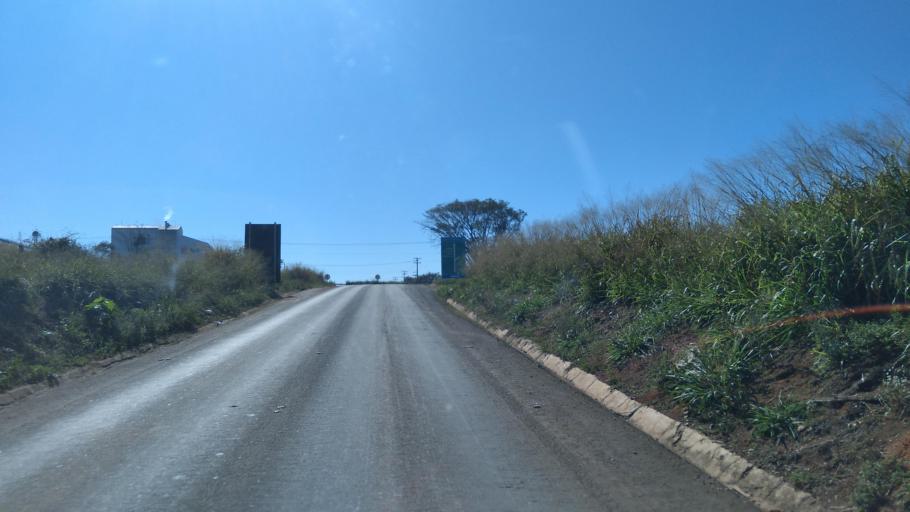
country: BR
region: Goias
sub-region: Mineiros
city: Mineiros
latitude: -17.5776
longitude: -52.5207
